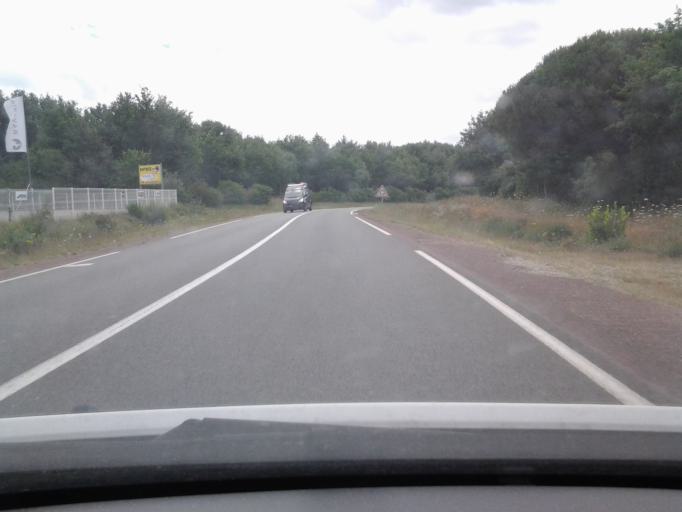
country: FR
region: Pays de la Loire
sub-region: Departement de la Vendee
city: Les Clouzeaux
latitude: 46.6498
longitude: -1.5091
